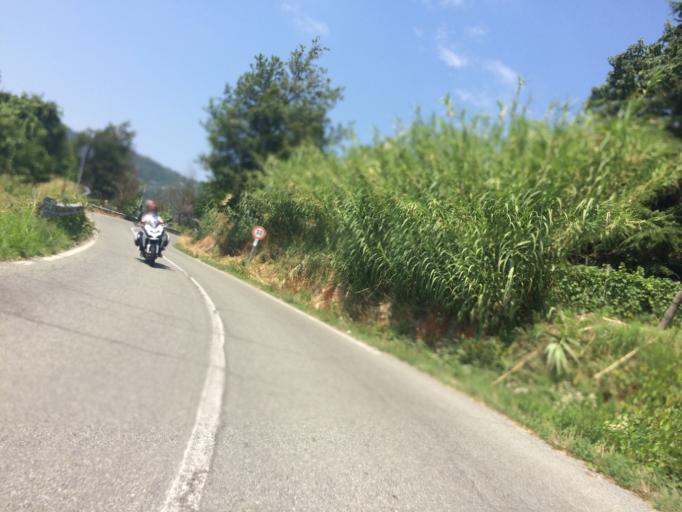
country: IT
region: Piedmont
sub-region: Provincia di Alessandria
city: Cartosio
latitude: 44.6125
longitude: 8.4163
